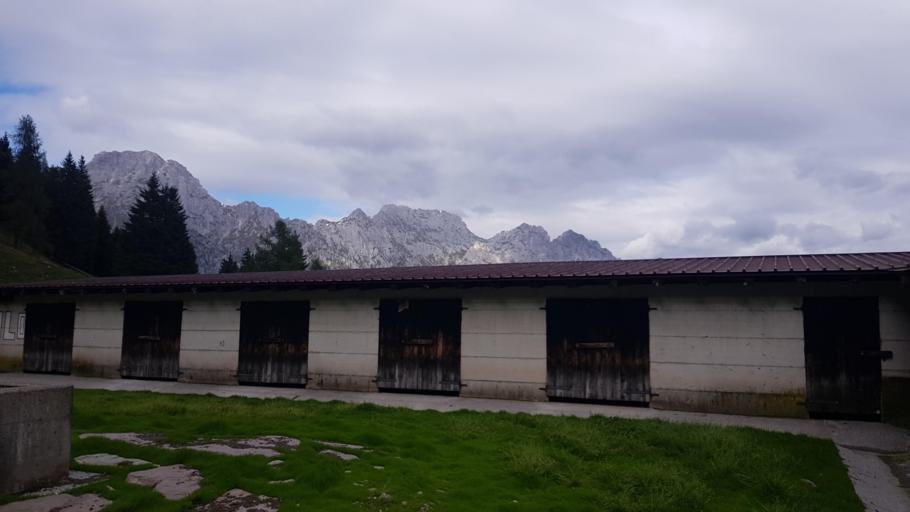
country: IT
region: Friuli Venezia Giulia
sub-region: Provincia di Udine
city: Sauris di Sotto
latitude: 46.5038
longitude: 12.7380
